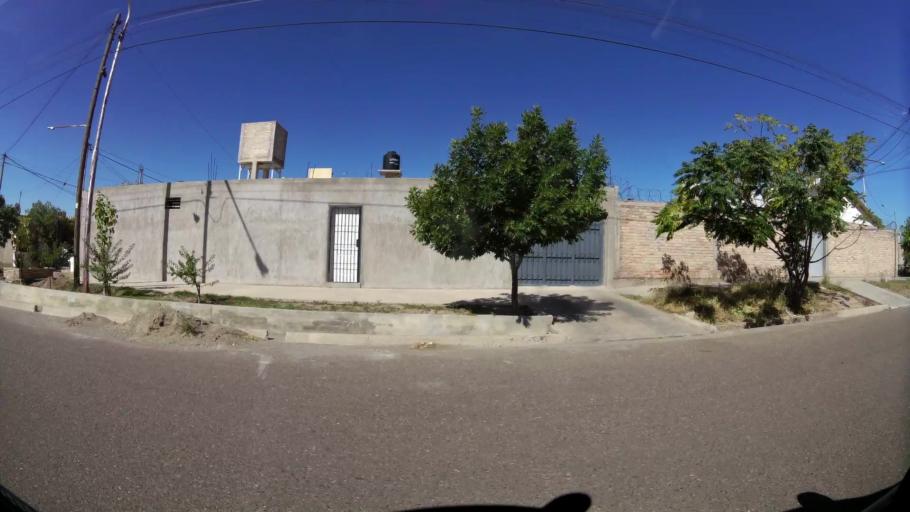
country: AR
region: Mendoza
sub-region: Departamento de Godoy Cruz
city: Godoy Cruz
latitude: -32.9509
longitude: -68.8171
